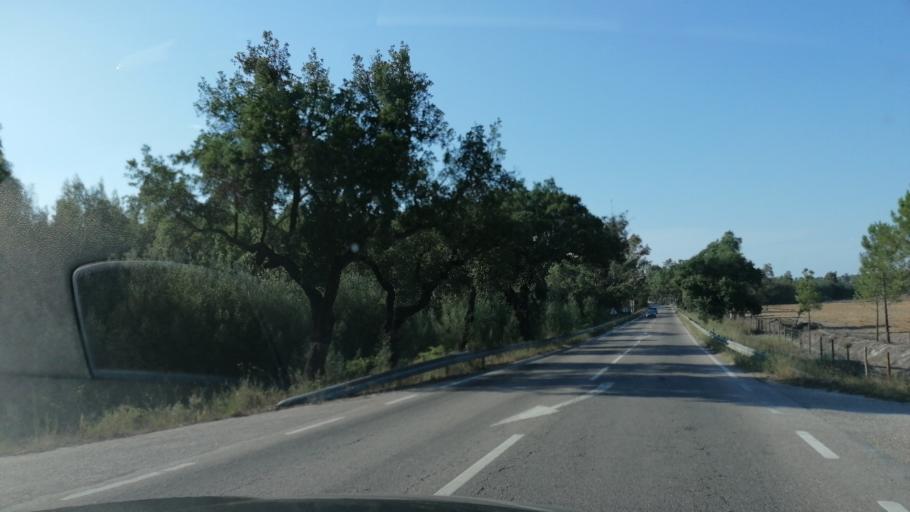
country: PT
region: Santarem
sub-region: Coruche
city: Coruche
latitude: 38.9888
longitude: -8.5524
